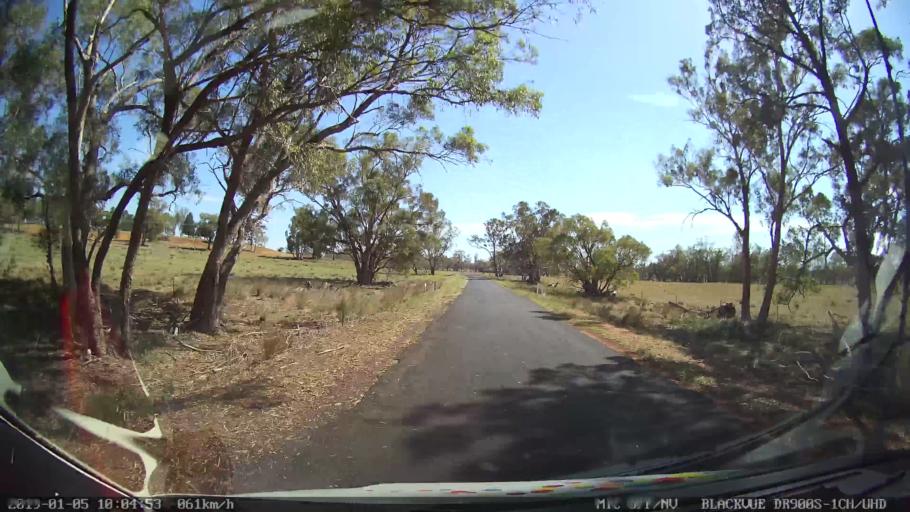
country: AU
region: New South Wales
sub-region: Gilgandra
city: Gilgandra
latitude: -31.6712
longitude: 148.8624
